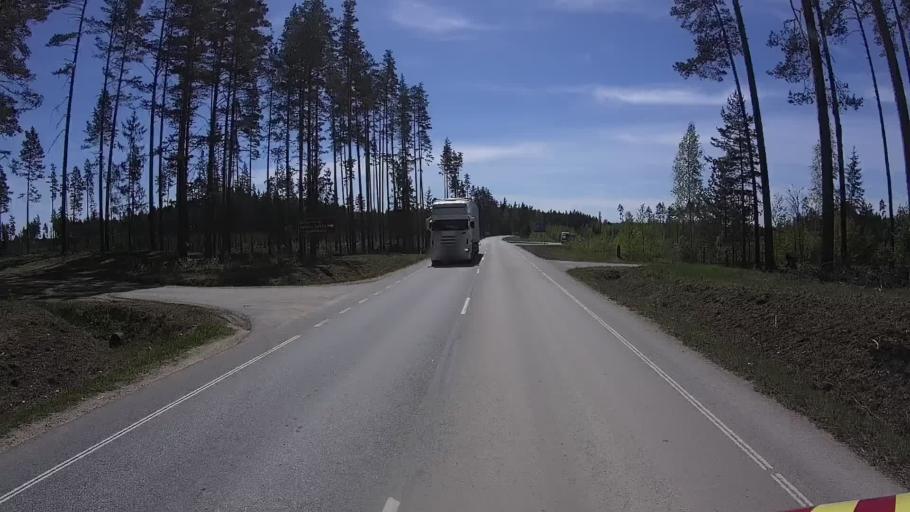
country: EE
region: Polvamaa
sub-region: Polva linn
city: Polva
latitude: 57.9232
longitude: 27.1825
